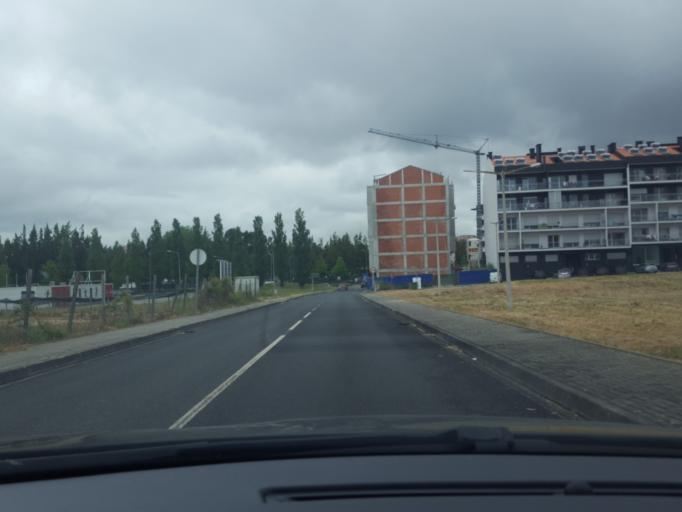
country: PT
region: Leiria
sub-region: Leiria
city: Leiria
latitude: 39.7350
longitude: -8.7933
